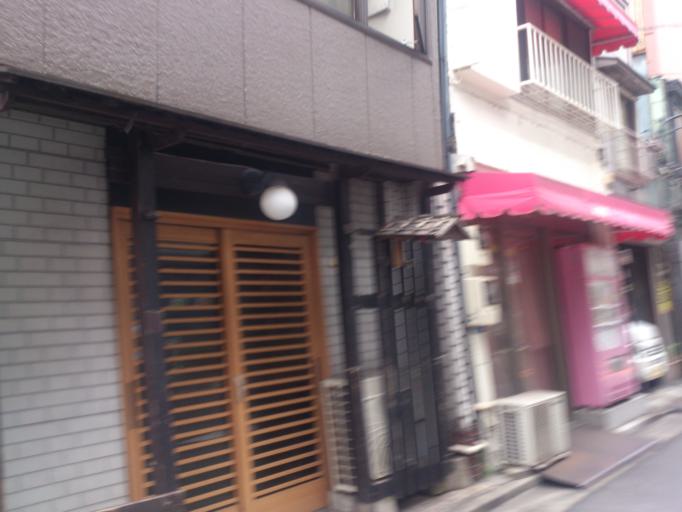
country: JP
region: Tokyo
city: Tokyo
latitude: 35.6846
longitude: 139.7831
